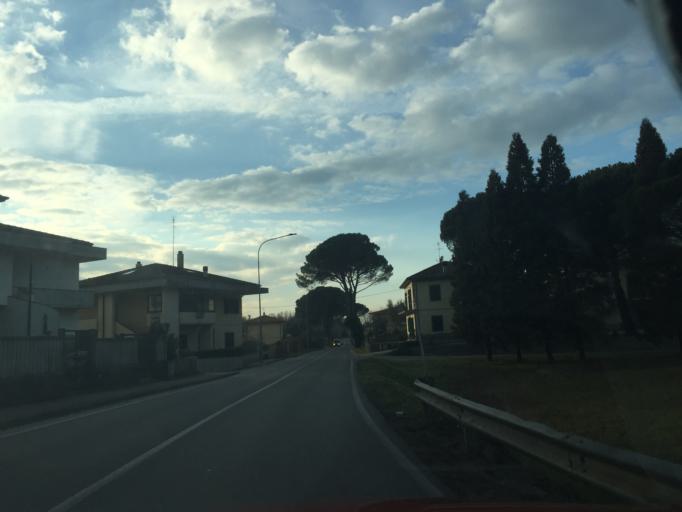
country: IT
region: Tuscany
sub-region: Provincia di Pistoia
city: Lamporecchio
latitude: 43.8173
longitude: 10.8901
